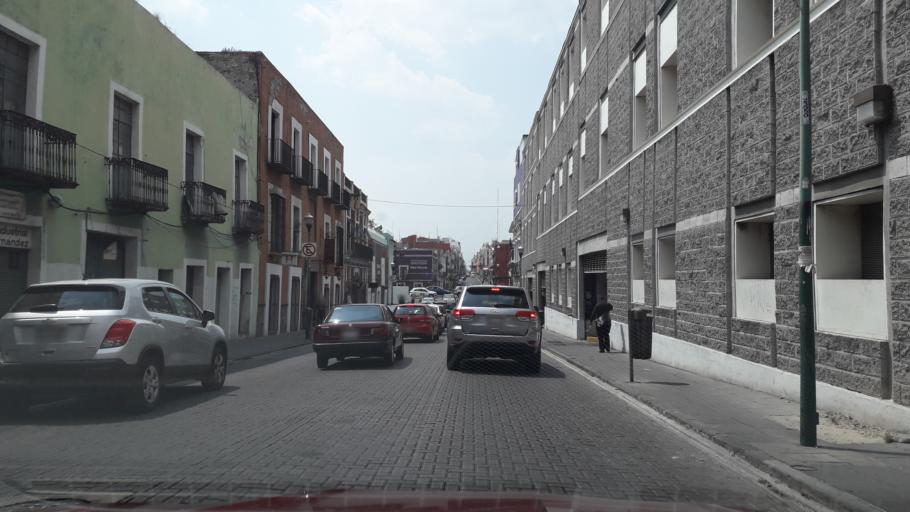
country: MX
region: Puebla
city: Puebla
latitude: 19.0418
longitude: -98.1915
